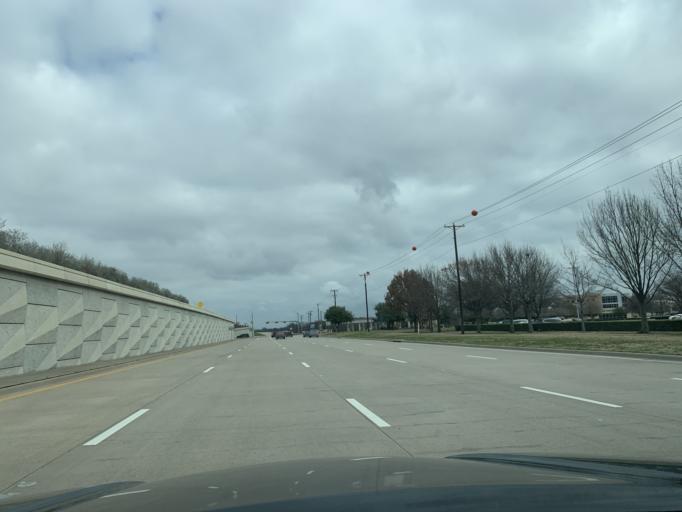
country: US
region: Texas
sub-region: Collin County
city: Fairview
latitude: 33.1610
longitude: -96.6379
